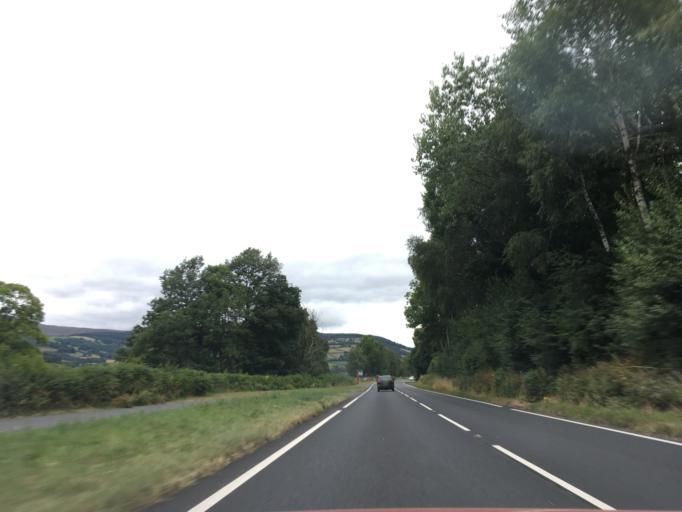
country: GB
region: Wales
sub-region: Blaenau Gwent
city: Brynmawr
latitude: 51.8942
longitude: -3.2616
